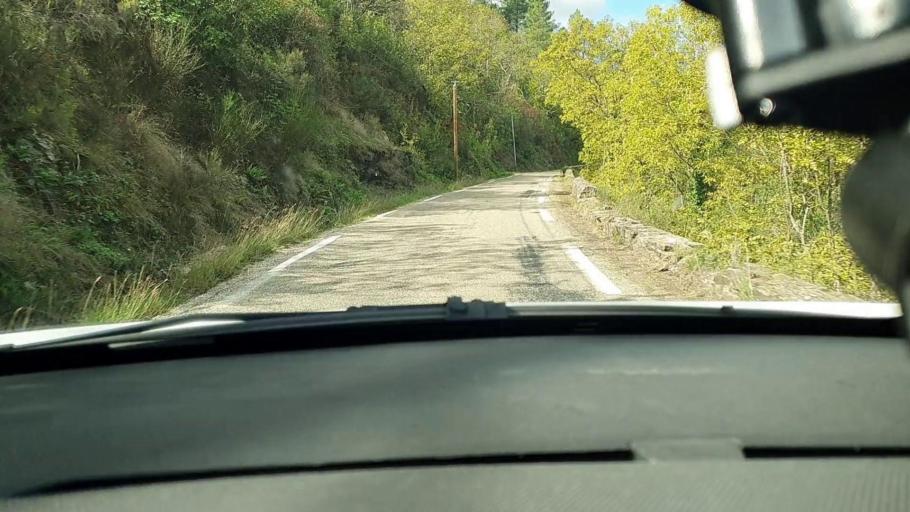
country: FR
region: Languedoc-Roussillon
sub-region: Departement du Gard
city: Besseges
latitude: 44.2986
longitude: 4.0302
